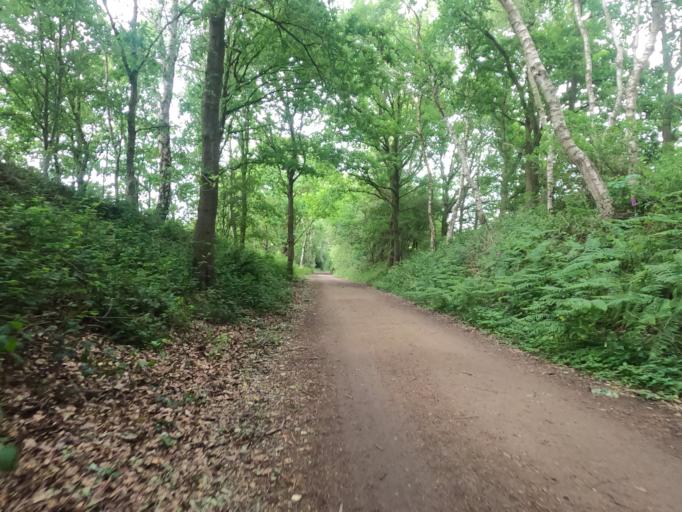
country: GB
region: England
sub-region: Cheshire West and Chester
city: Cuddington
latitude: 53.2330
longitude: -2.6161
